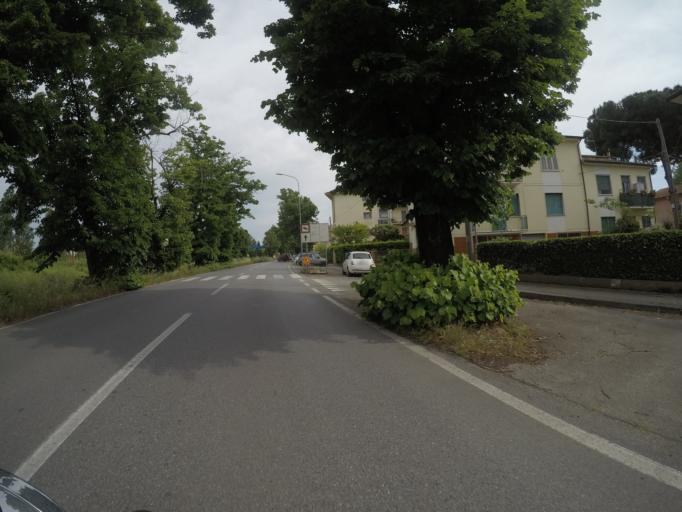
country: IT
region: Tuscany
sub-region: Province of Pisa
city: Madonna dell'Acqua
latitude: 43.7299
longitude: 10.3879
